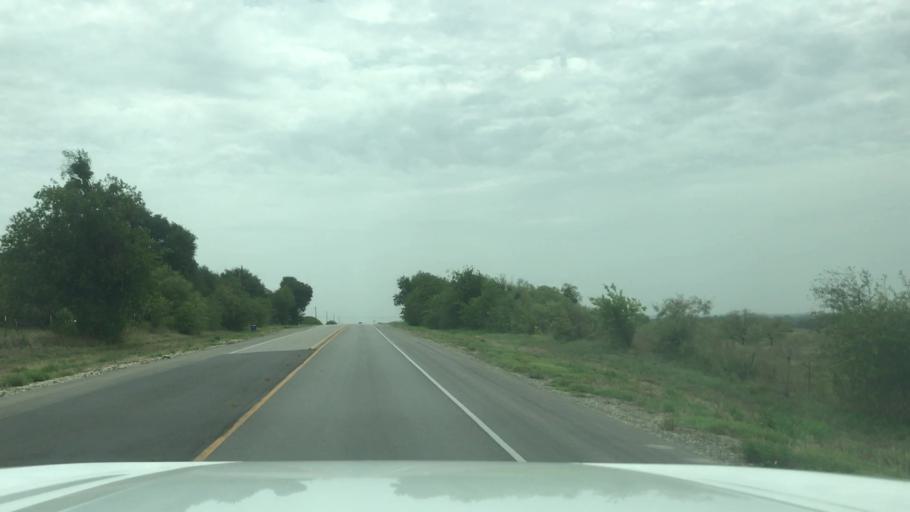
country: US
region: Texas
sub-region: Erath County
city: Dublin
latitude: 32.0799
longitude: -98.2429
